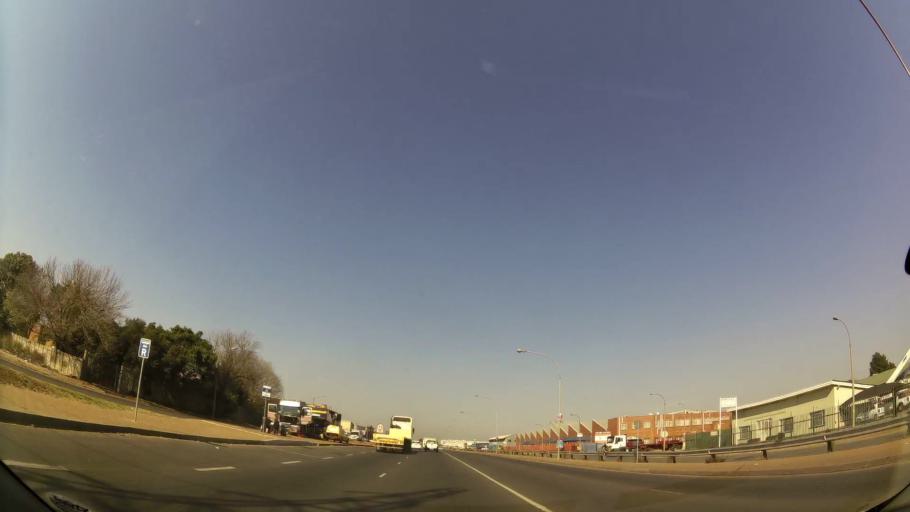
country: ZA
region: Gauteng
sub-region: City of Johannesburg Metropolitan Municipality
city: Modderfontein
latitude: -26.1424
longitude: 28.2020
